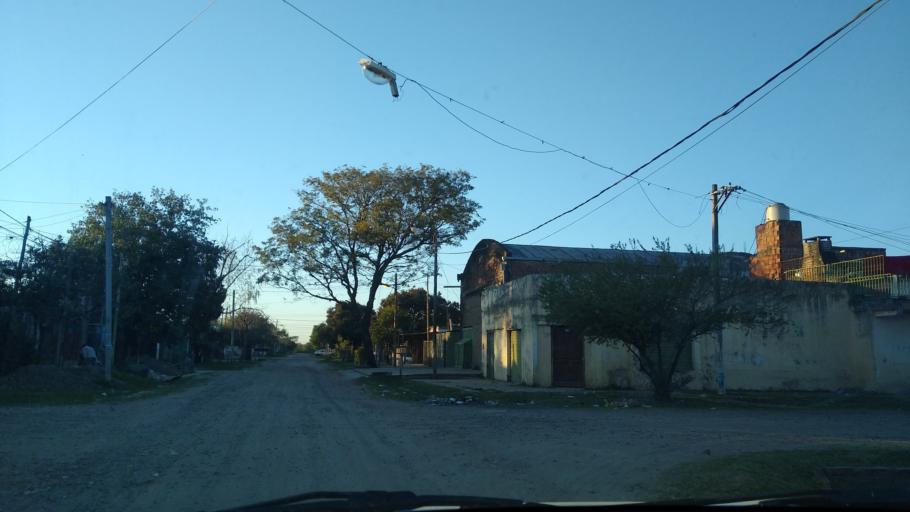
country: AR
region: Chaco
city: Resistencia
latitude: -27.4790
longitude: -58.9653
